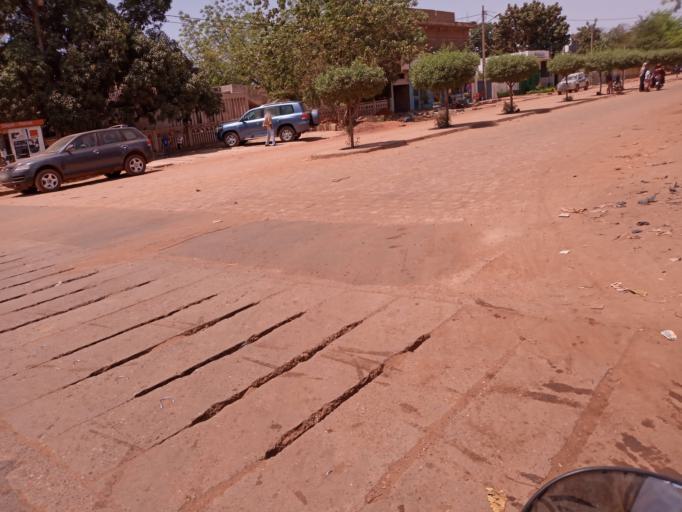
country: ML
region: Bamako
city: Bamako
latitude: 12.6632
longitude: -7.9494
